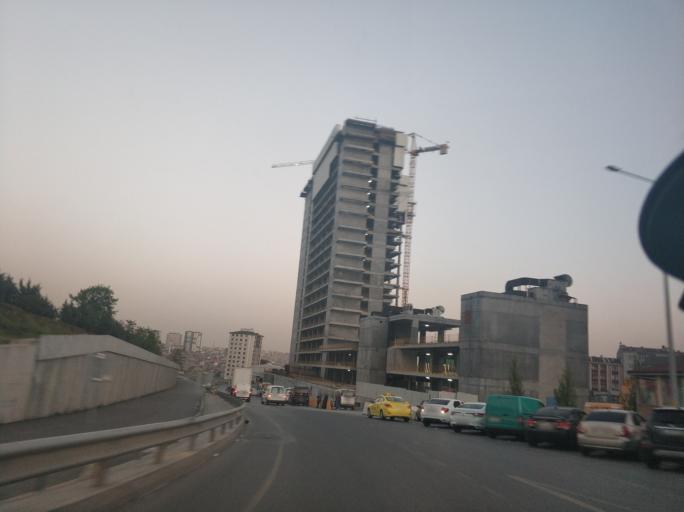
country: TR
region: Istanbul
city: Mahmutbey
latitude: 41.0596
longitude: 28.8427
